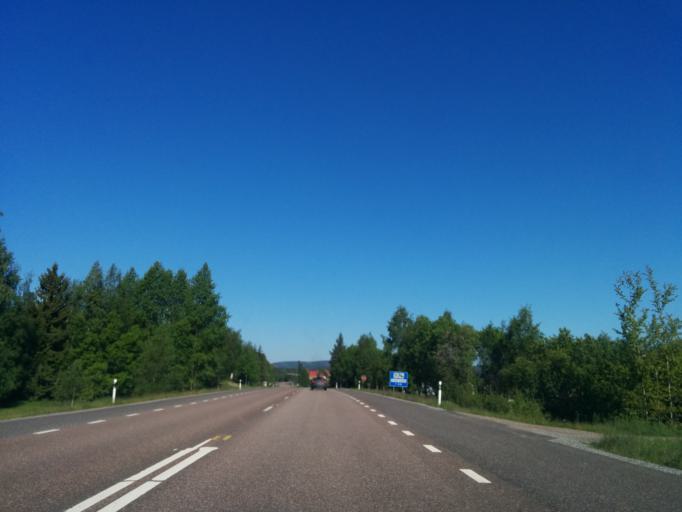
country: SE
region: Vaesternorrland
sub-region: Kramfors Kommun
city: Kramfors
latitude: 62.9054
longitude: 17.8257
